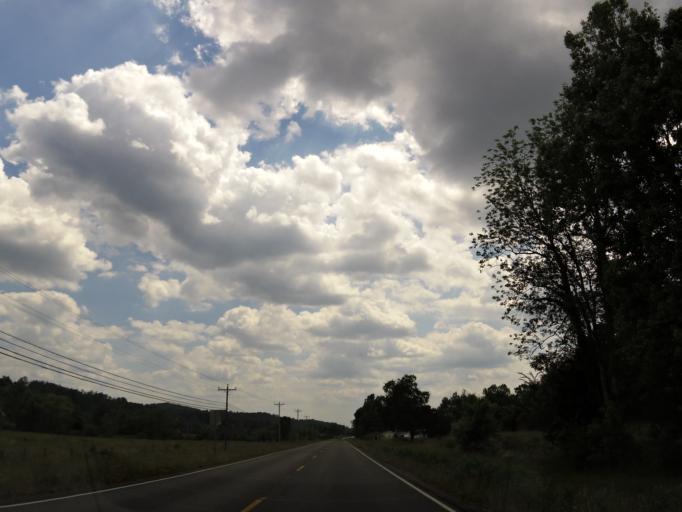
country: US
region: Tennessee
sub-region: Bledsoe County
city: Pikeville
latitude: 35.5158
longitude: -85.2800
